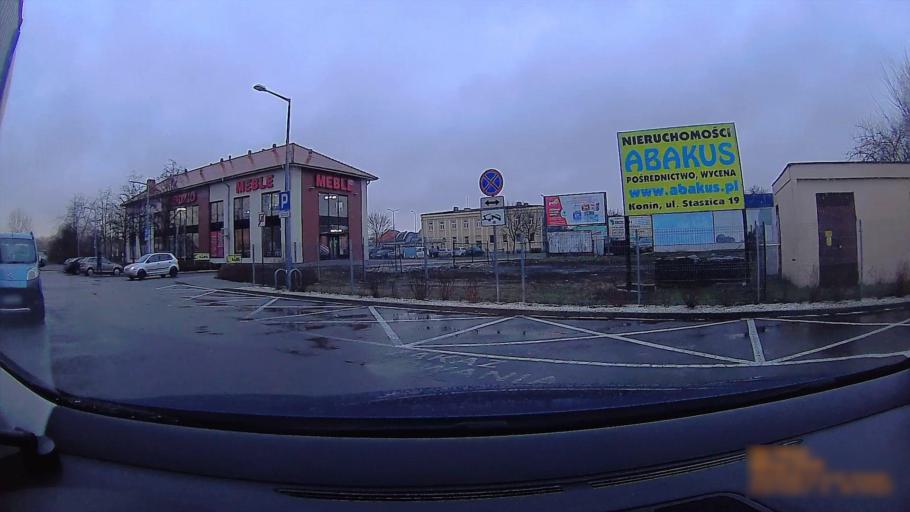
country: PL
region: Greater Poland Voivodeship
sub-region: Konin
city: Konin
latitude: 52.2079
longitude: 18.2531
